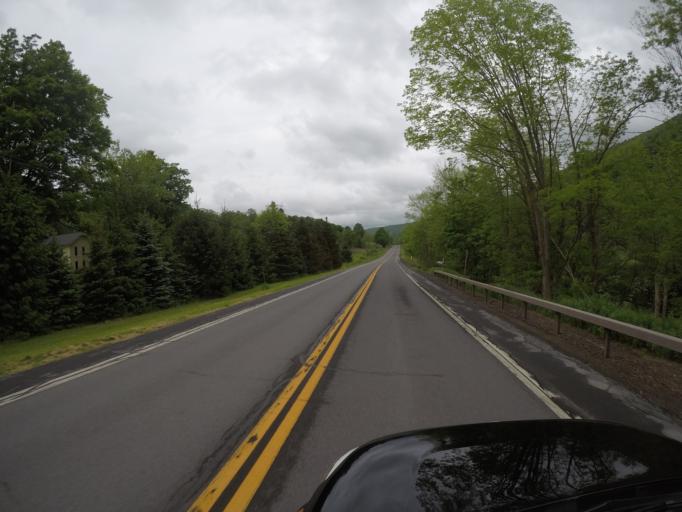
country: US
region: New York
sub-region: Delaware County
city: Delhi
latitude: 42.2529
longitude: -74.8495
